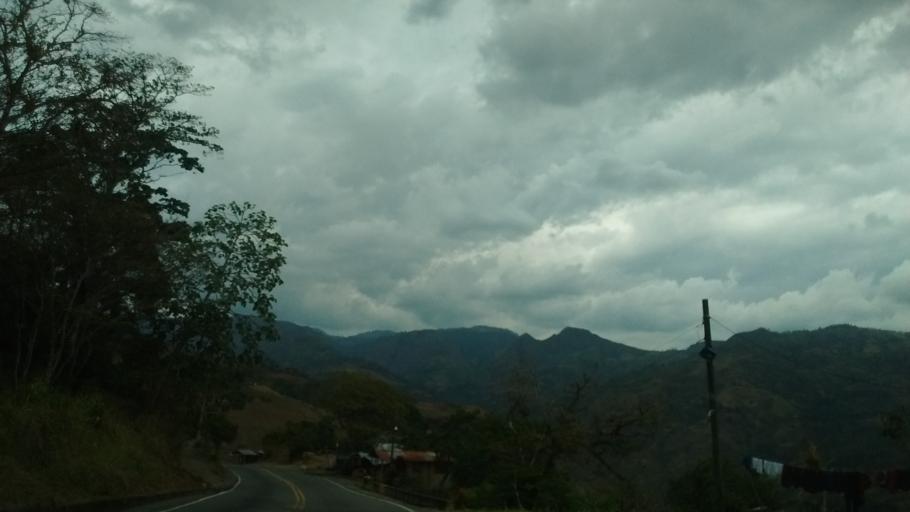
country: CO
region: Cauca
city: Rosas
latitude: 2.2872
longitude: -76.7086
